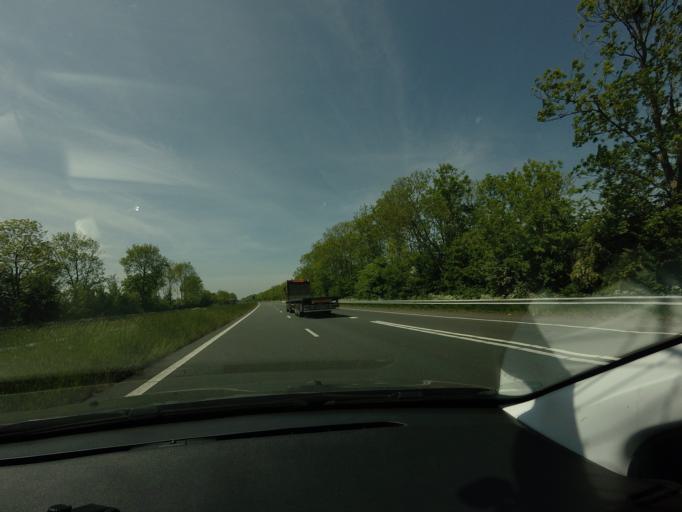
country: NL
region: Friesland
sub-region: Sudwest Fryslan
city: Bolsward
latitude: 53.0568
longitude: 5.5306
